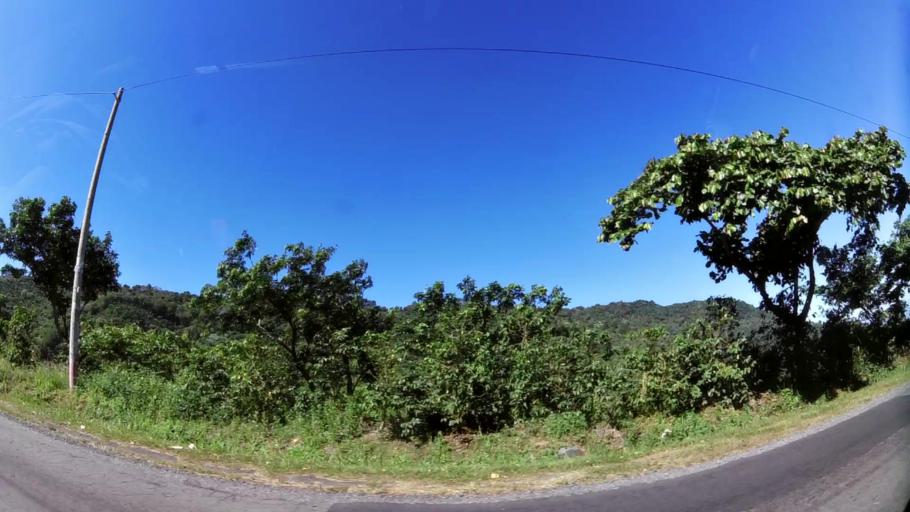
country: SV
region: Ahuachapan
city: Concepcion de Ataco
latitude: 13.8769
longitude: -89.8449
